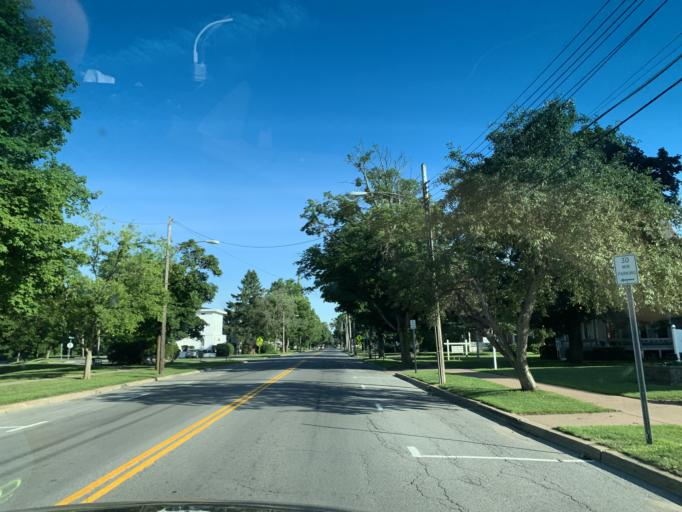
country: US
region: New York
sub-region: Madison County
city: Oneida
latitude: 43.0922
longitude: -75.6502
